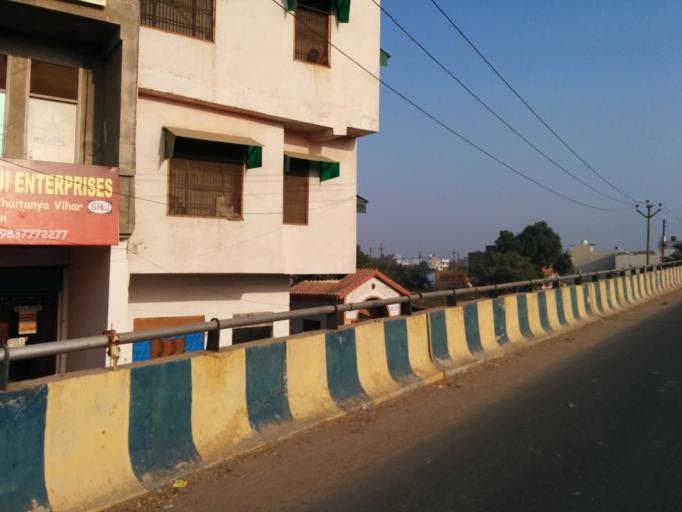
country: IN
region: Uttar Pradesh
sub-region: Mathura
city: Vrindavan
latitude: 27.5650
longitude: 77.6777
